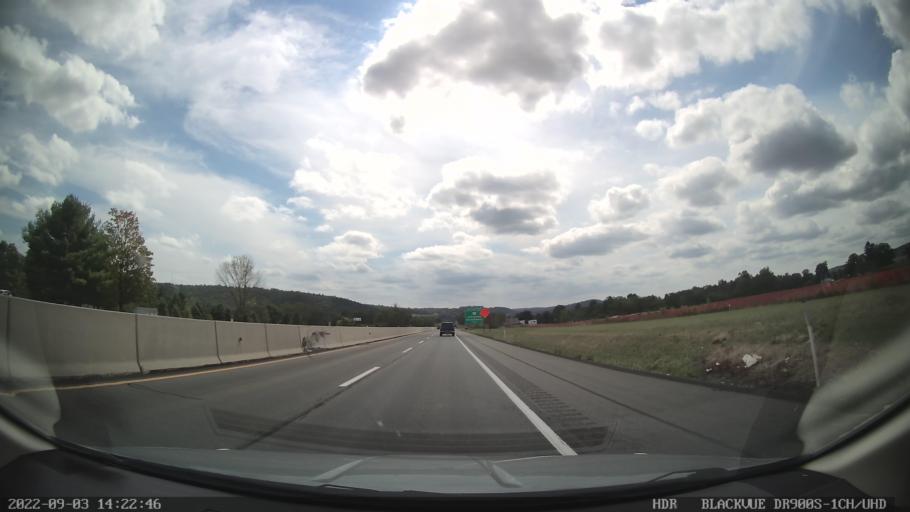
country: US
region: Pennsylvania
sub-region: Carbon County
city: Weissport East
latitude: 40.8516
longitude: -75.6552
